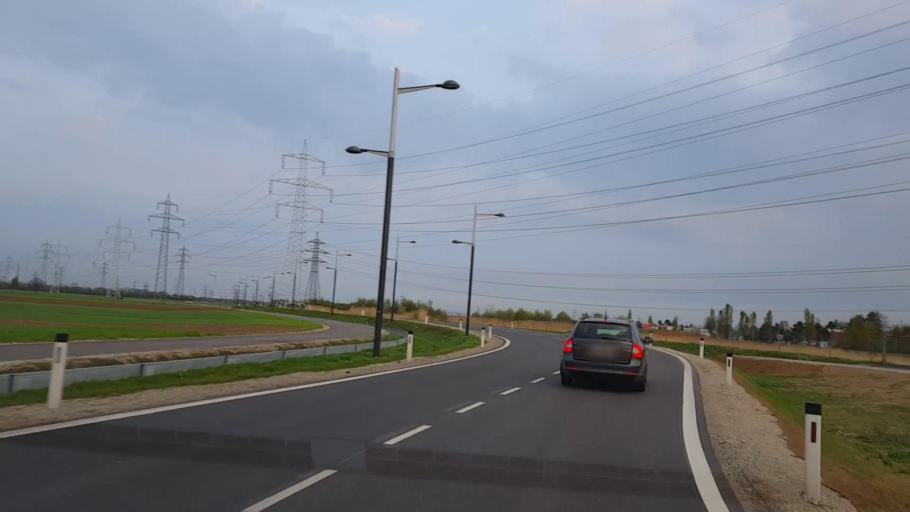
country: AT
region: Lower Austria
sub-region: Politischer Bezirk Wien-Umgebung
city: Leopoldsdorf
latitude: 48.1286
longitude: 16.3892
